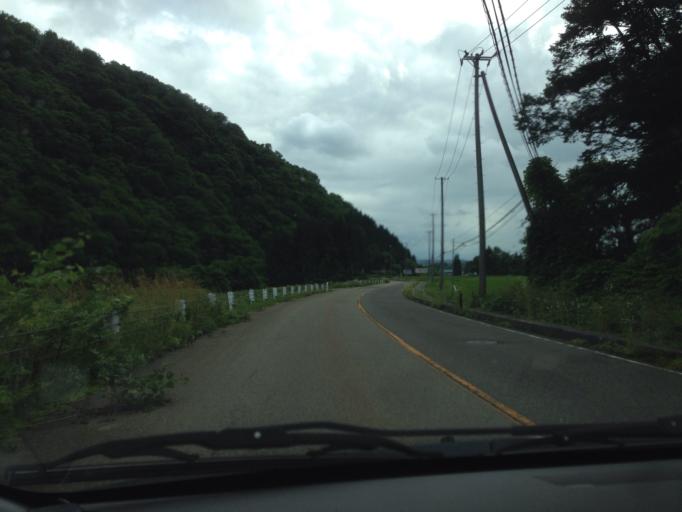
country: JP
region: Fukushima
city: Kitakata
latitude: 37.7397
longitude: 139.8878
